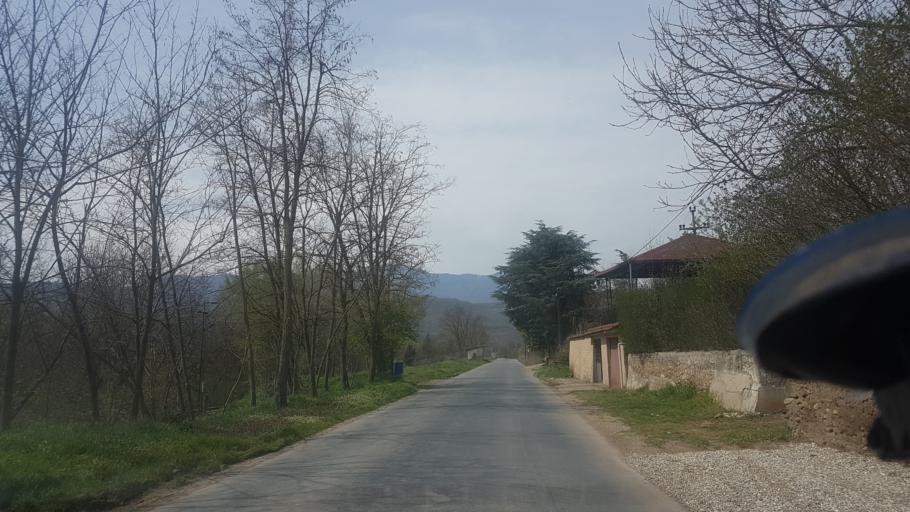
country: MK
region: Zelenikovo
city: Zelenikovo
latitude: 41.8950
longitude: 21.6016
